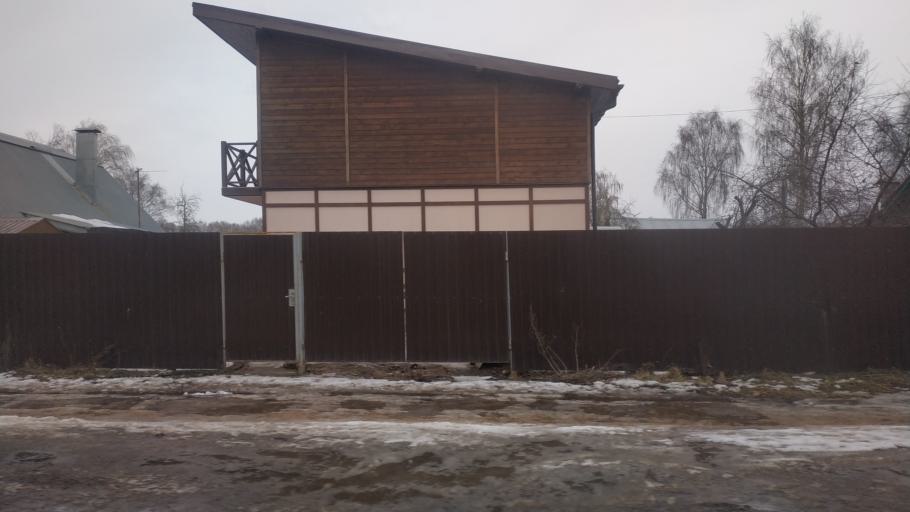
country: RU
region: Tverskaya
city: Tver
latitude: 56.8800
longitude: 35.8913
